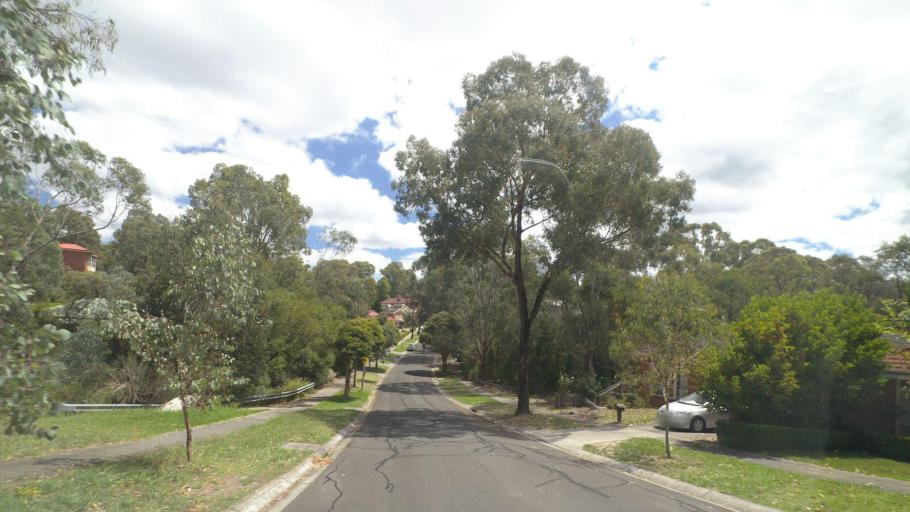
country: AU
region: Victoria
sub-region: Maroondah
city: Warranwood
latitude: -37.7787
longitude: 145.2416
